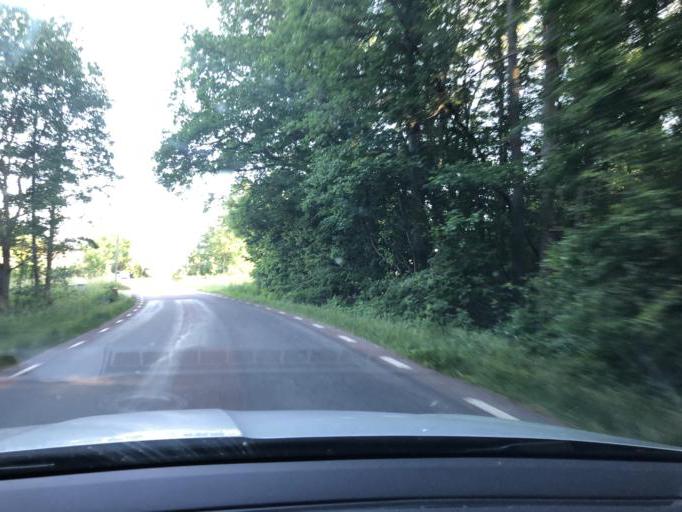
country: SE
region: Blekinge
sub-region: Solvesborgs Kommun
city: Soelvesborg
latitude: 56.1390
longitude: 14.6070
